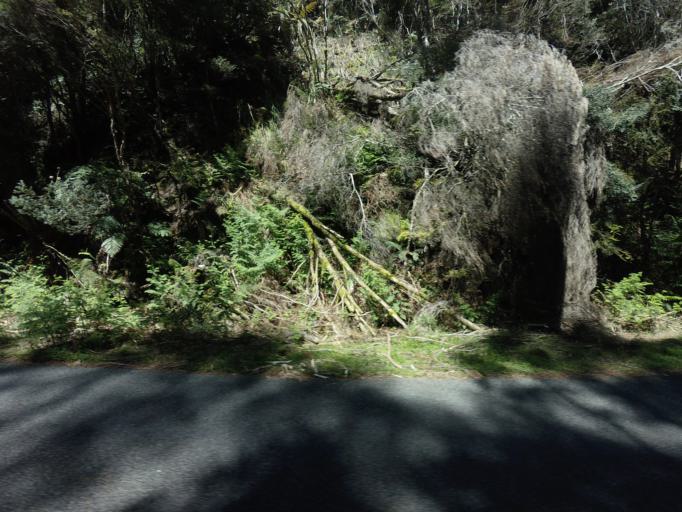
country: AU
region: Tasmania
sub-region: West Coast
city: Queenstown
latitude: -42.7684
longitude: 146.0088
